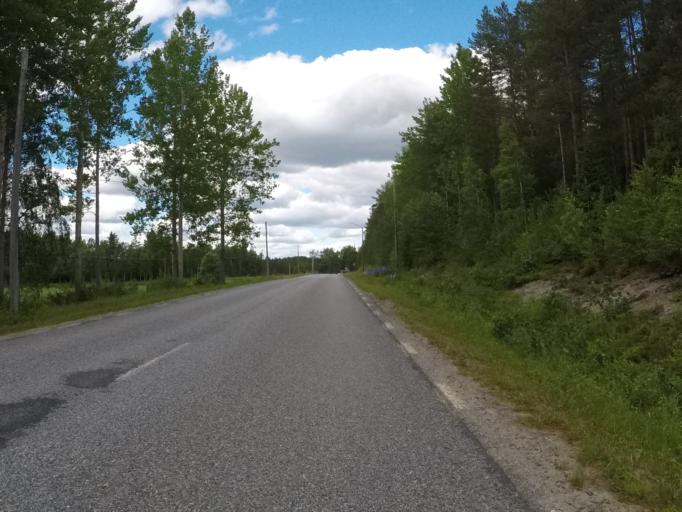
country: SE
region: Vaesterbotten
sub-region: Robertsfors Kommun
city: Robertsfors
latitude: 63.9956
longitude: 20.8075
